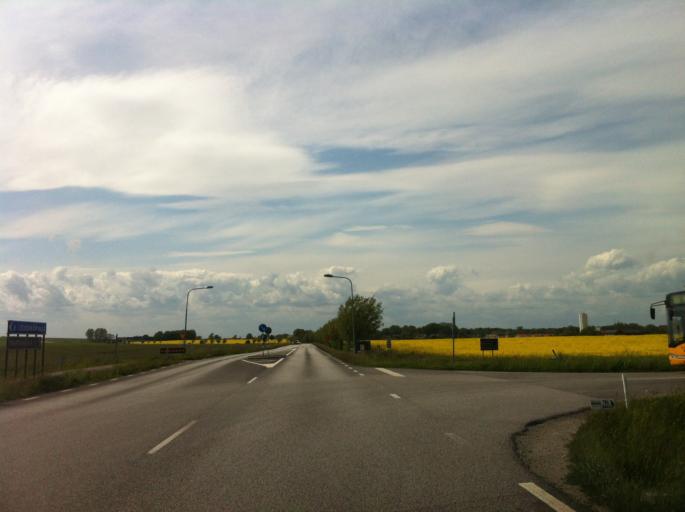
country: SE
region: Skane
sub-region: Kavlinge Kommun
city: Hofterup
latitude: 55.7661
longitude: 12.9739
